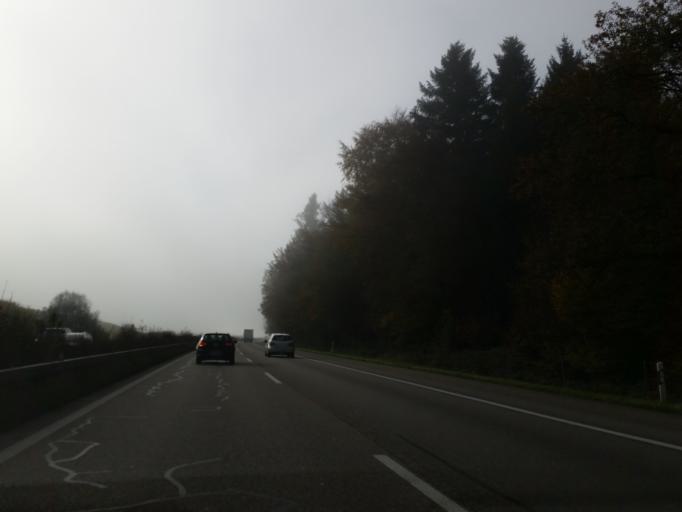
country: CH
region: Bern
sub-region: Emmental District
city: Koppigen
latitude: 47.1459
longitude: 7.5909
